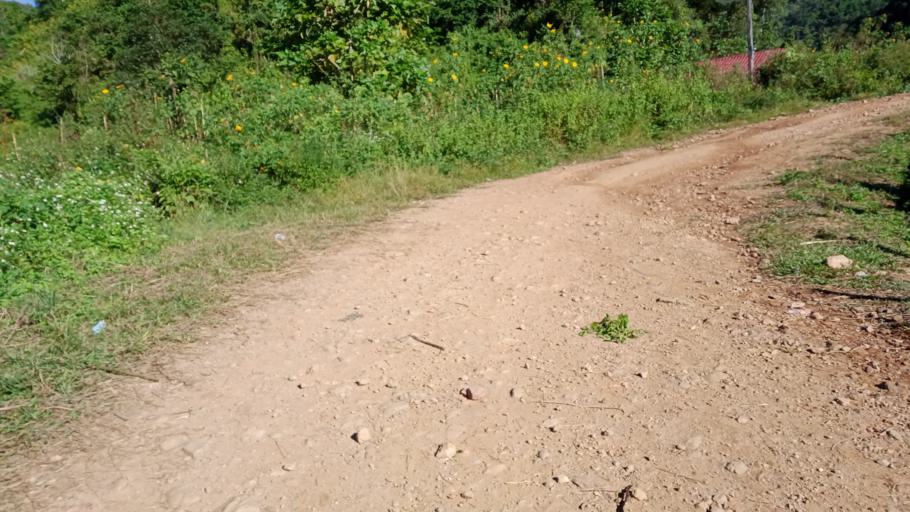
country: LA
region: Xiangkhoang
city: Phonsavan
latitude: 19.1170
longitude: 102.9097
